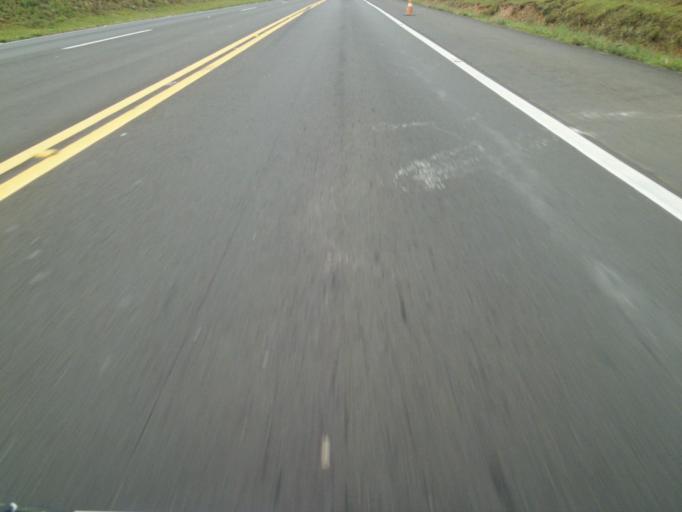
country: BR
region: Parana
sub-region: Palmeira
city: Palmeira
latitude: -25.4763
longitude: -49.8477
